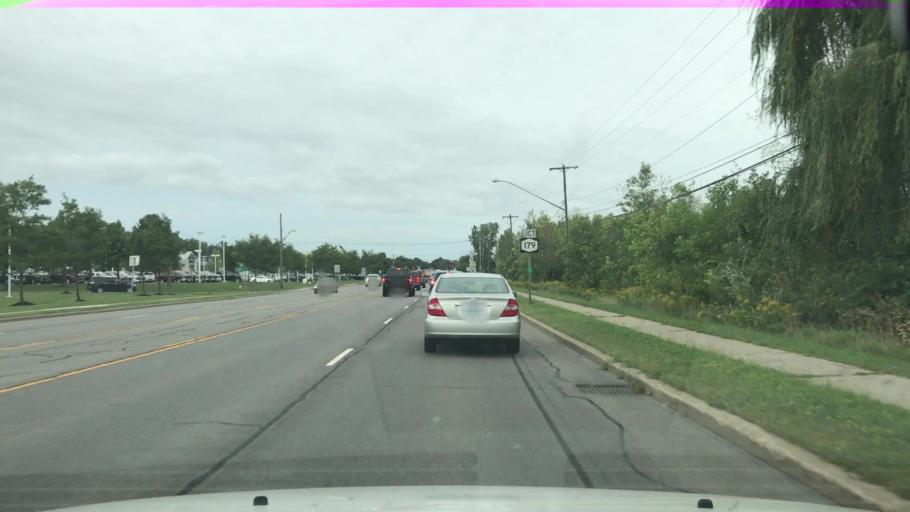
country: US
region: New York
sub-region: Erie County
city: Orchard Park
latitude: 42.7912
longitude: -78.7582
